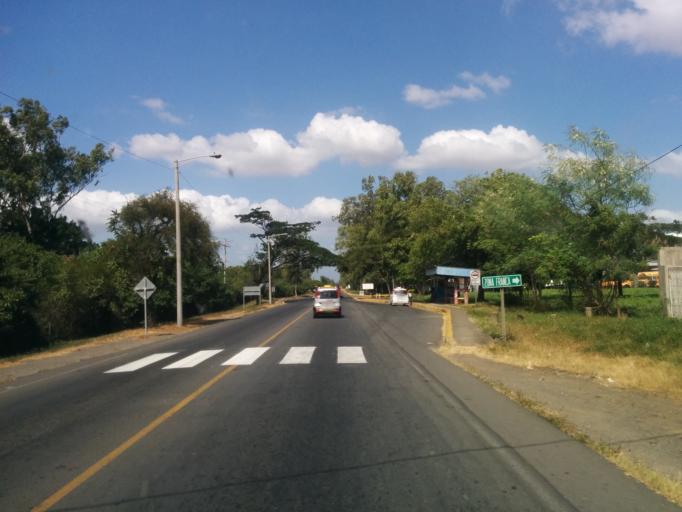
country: NI
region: Masaya
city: Nindiri
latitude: 12.0002
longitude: -86.1041
